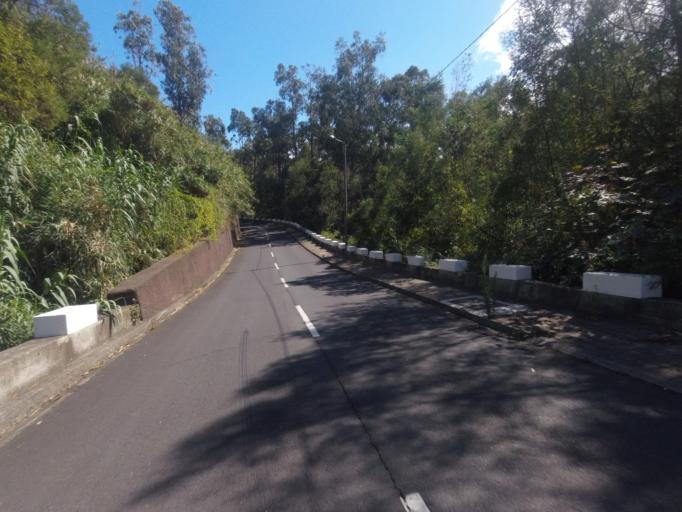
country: PT
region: Madeira
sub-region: Ribeira Brava
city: Campanario
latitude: 32.6855
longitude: -17.0408
